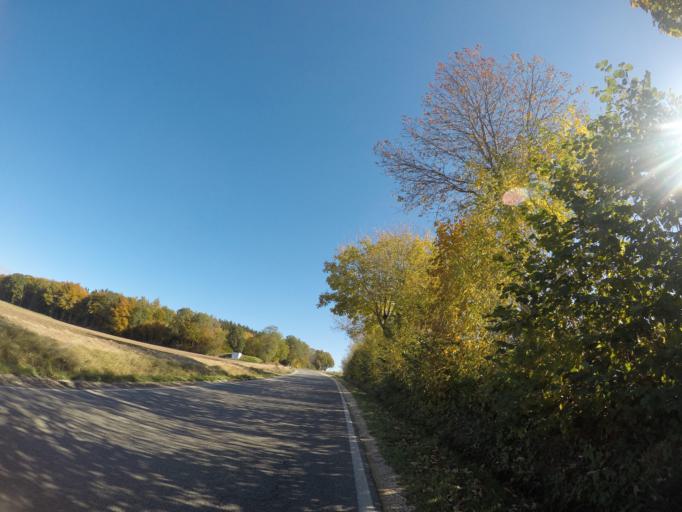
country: DE
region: Baden-Wuerttemberg
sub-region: Tuebingen Region
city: Saulgau
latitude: 48.0485
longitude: 9.5255
